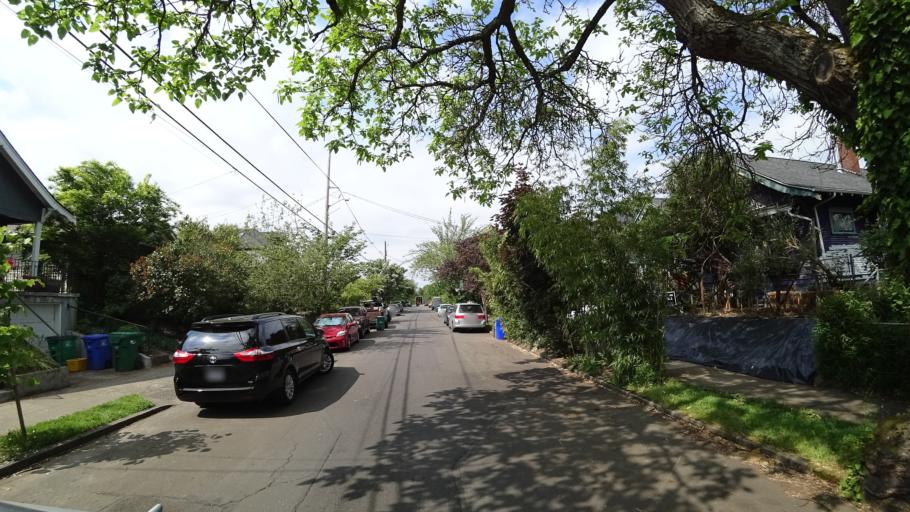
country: US
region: Oregon
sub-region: Multnomah County
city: Portland
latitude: 45.5568
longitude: -122.6488
